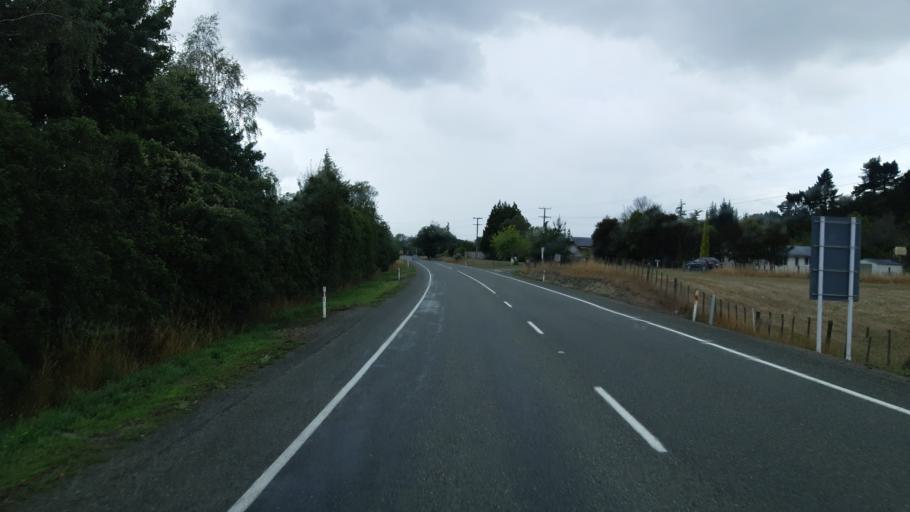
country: NZ
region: Tasman
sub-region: Tasman District
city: Wakefield
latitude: -41.4104
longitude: 173.0233
